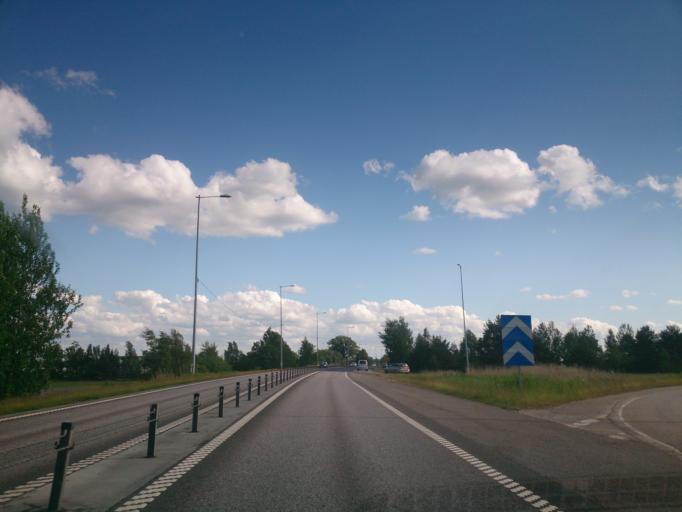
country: SE
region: OEstergoetland
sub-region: Norrkopings Kommun
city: Jursla
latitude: 58.6584
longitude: 16.1698
